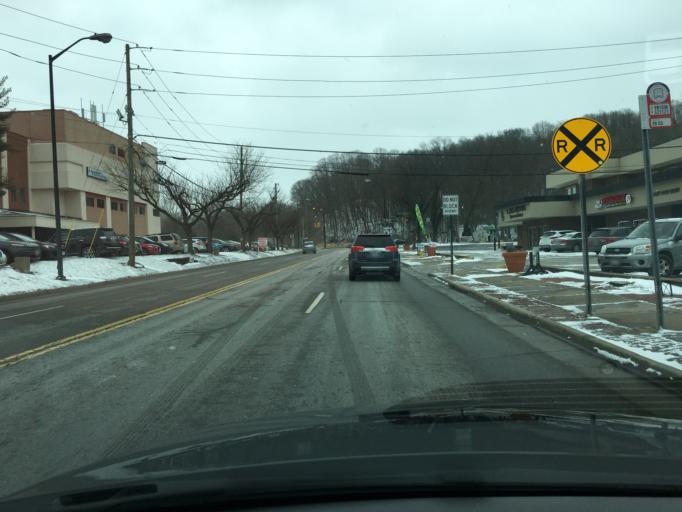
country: US
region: Ohio
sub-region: Summit County
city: Fairlawn
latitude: 41.1338
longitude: -81.5501
